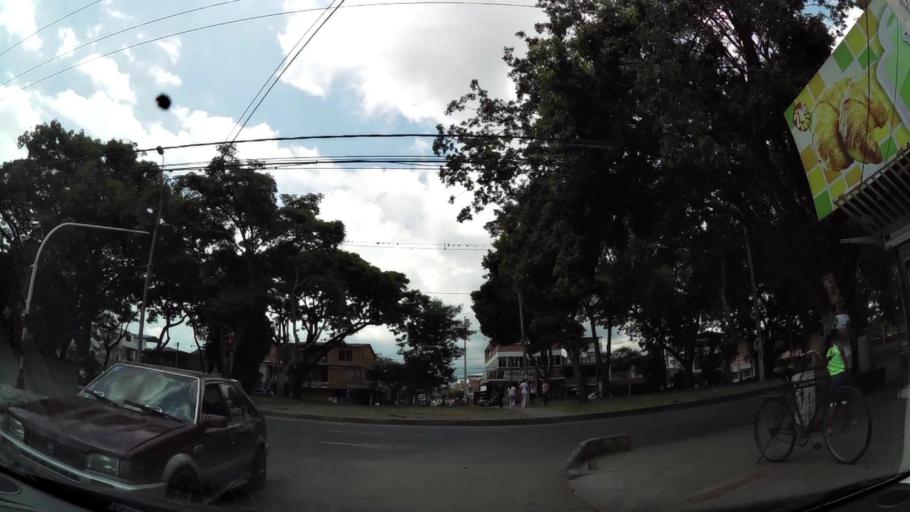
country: CO
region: Valle del Cauca
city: Cali
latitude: 3.4747
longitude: -76.4828
